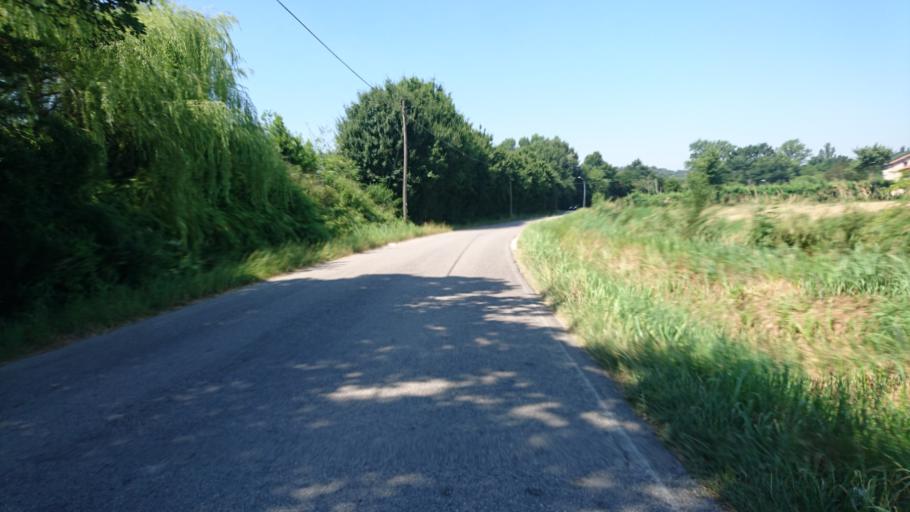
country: IT
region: Veneto
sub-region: Provincia di Padova
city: Montemerlo
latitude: 45.3902
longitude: 11.6884
